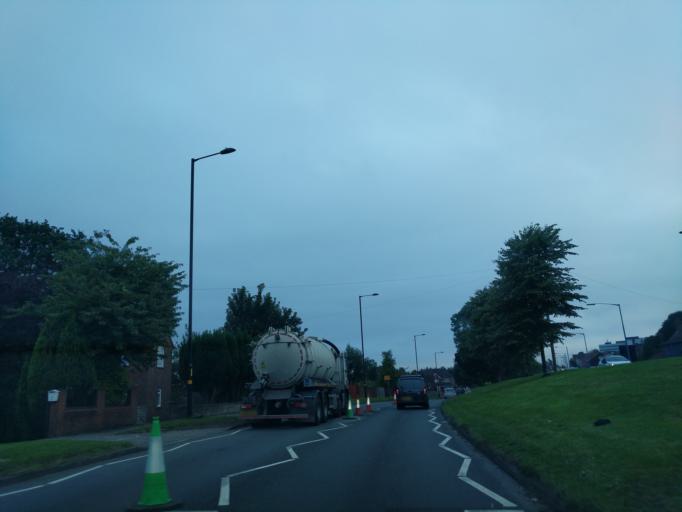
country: GB
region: England
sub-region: Sandwell
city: Smethwick
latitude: 52.4674
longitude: -1.9771
